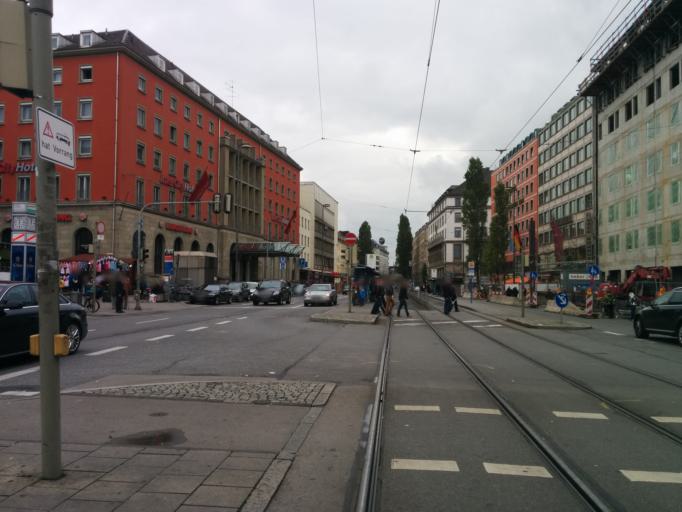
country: DE
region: Bavaria
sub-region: Upper Bavaria
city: Munich
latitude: 48.1393
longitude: 11.5584
